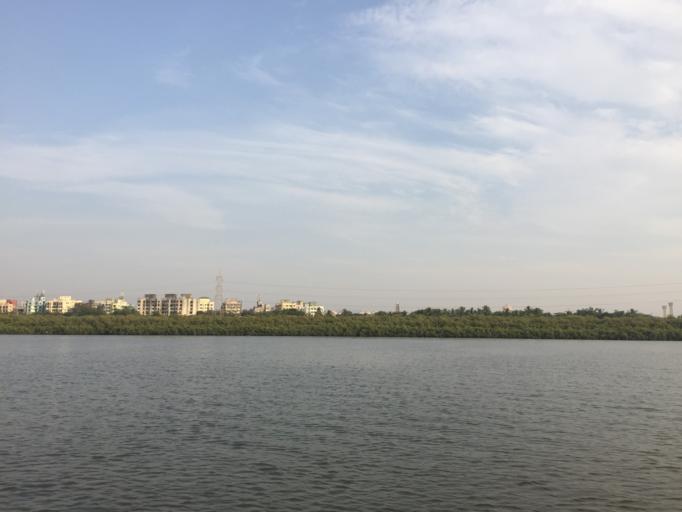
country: IN
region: Maharashtra
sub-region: Mumbai Suburban
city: Borivli
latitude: 19.2298
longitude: 72.8173
